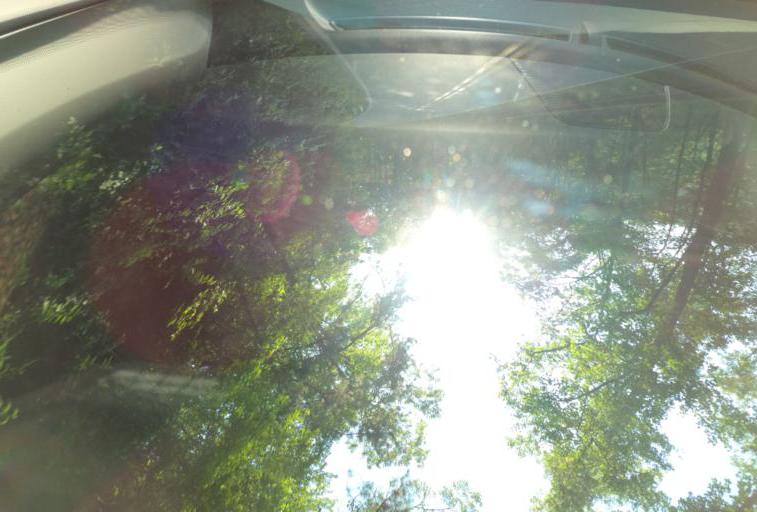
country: US
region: North Carolina
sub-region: Transylvania County
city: Brevard
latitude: 35.1664
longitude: -82.8417
